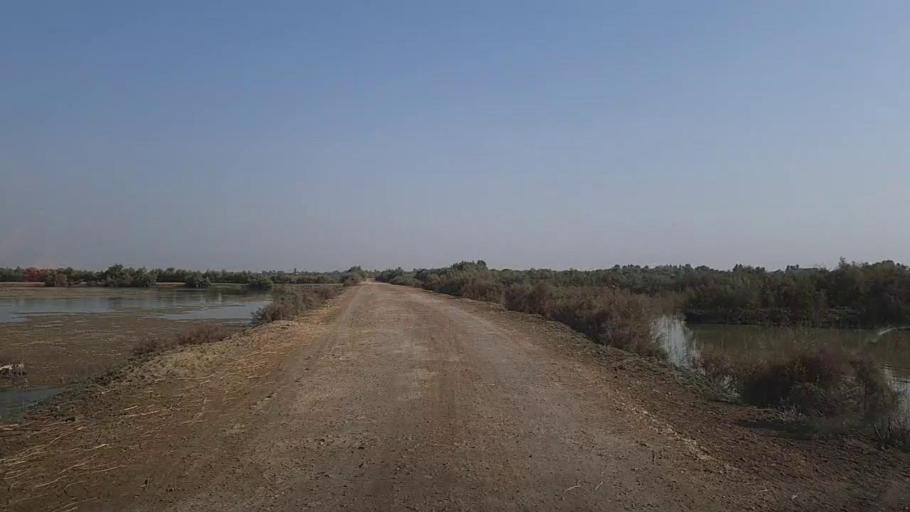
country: PK
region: Sindh
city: Kandhkot
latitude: 28.3591
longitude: 69.3306
